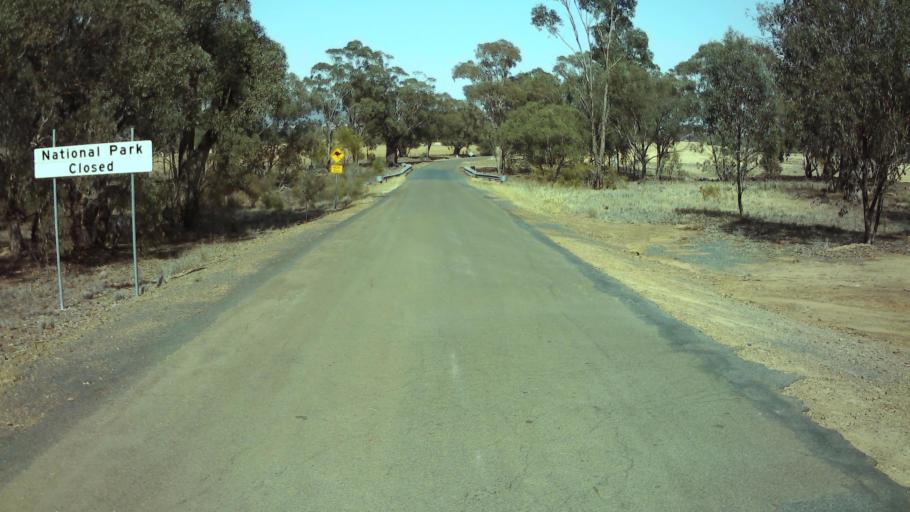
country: AU
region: New South Wales
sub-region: Weddin
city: Grenfell
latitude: -33.8698
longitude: 148.1122
